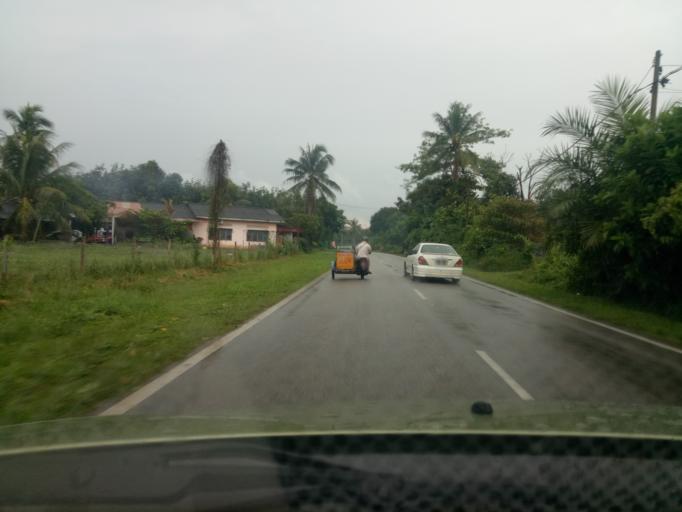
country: MY
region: Penang
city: Tasek Glugor
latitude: 5.5396
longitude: 100.5694
